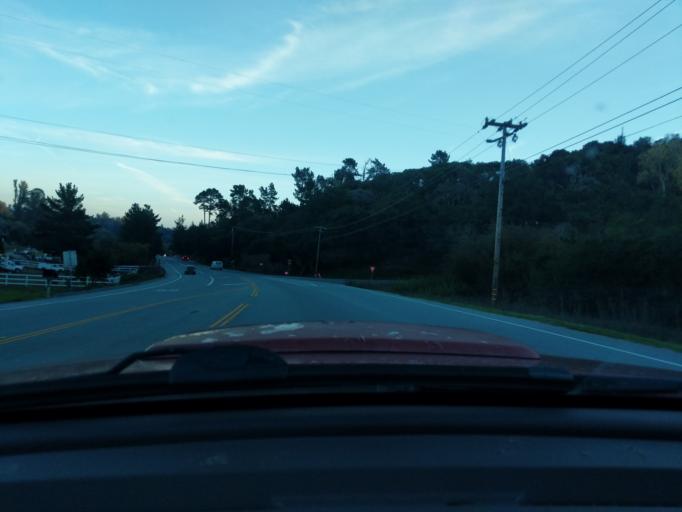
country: US
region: California
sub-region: Monterey County
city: Prunedale
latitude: 36.8091
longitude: -121.6727
